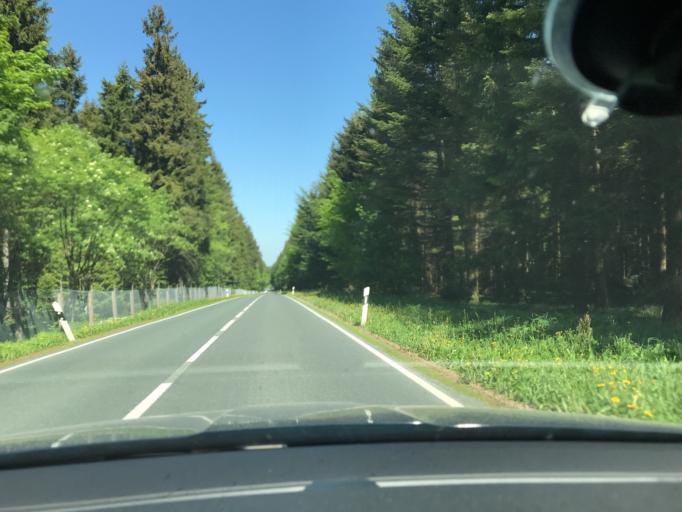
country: CZ
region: Ustecky
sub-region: Okres Chomutov
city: Vejprty
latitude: 50.4591
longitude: 12.9971
